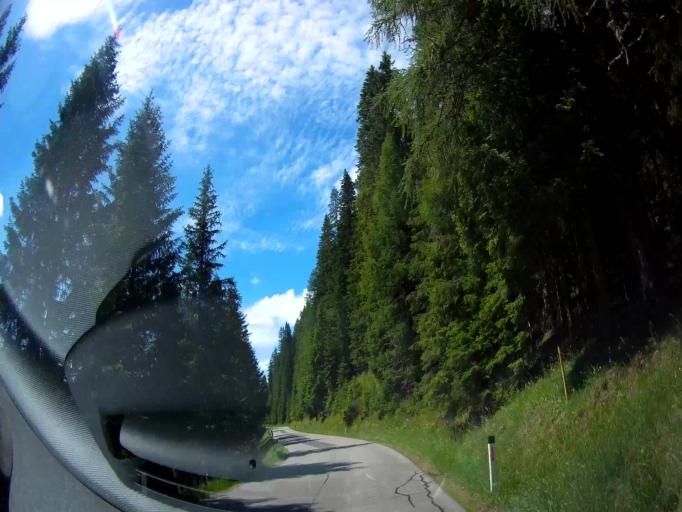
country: AT
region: Carinthia
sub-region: Politischer Bezirk Sankt Veit an der Glan
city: Glodnitz
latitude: 46.9383
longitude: 14.0412
